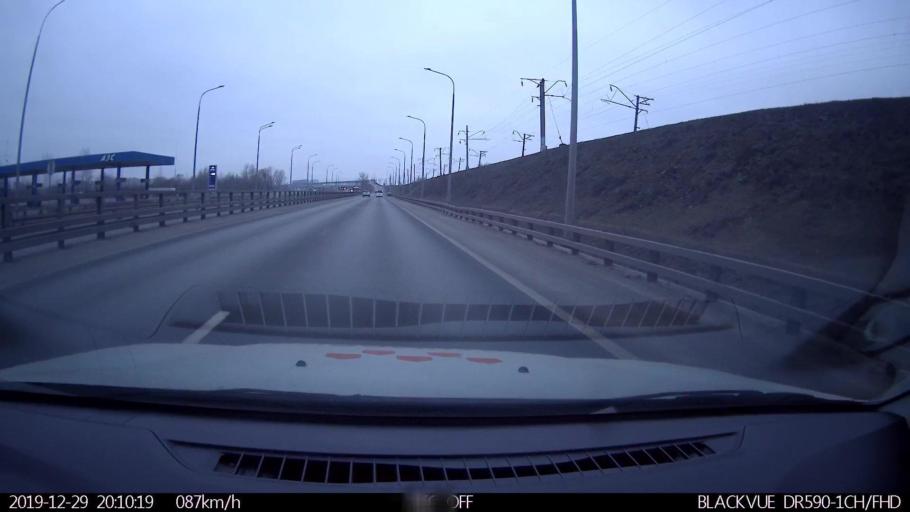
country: RU
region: Nizjnij Novgorod
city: Neklyudovo
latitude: 56.3663
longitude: 43.9376
